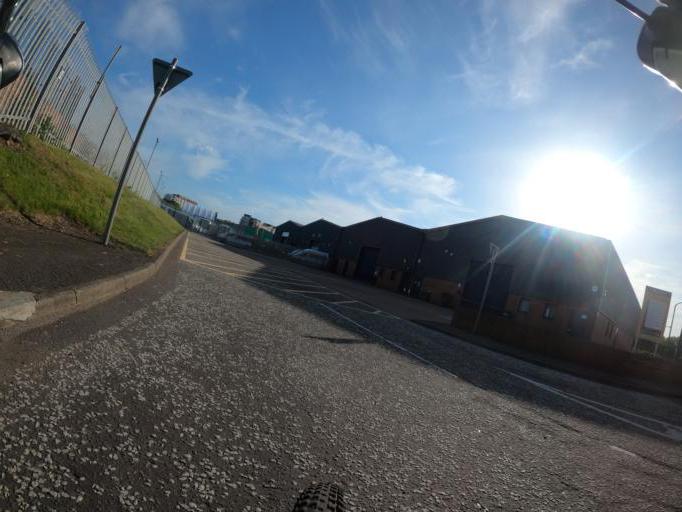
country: GB
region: Scotland
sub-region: Edinburgh
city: Edinburgh
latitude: 55.9841
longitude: -3.2298
